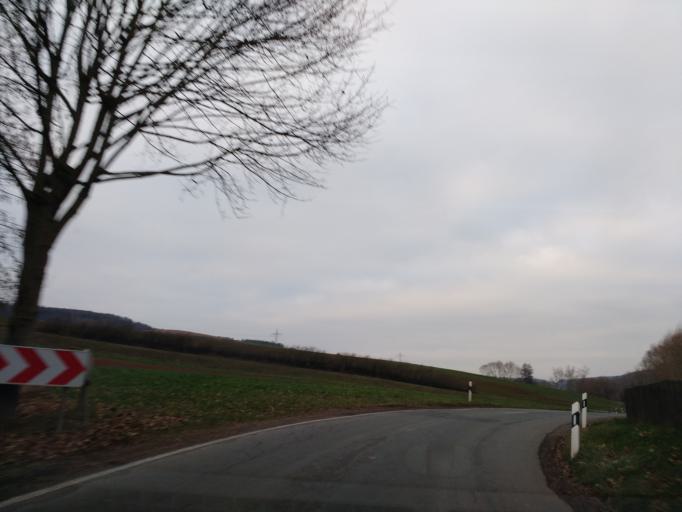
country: DE
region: Hesse
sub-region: Regierungsbezirk Kassel
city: Rotenburg an der Fulda
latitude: 51.0543
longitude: 9.7626
